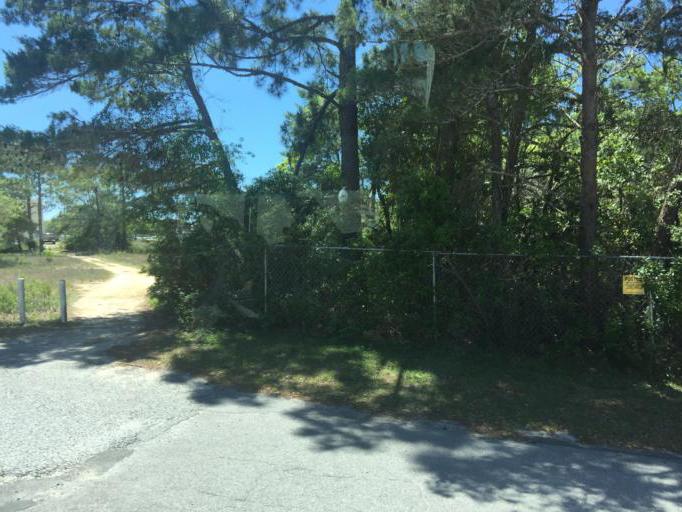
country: US
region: Florida
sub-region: Bay County
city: Laguna Beach
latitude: 30.2670
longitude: -85.9748
